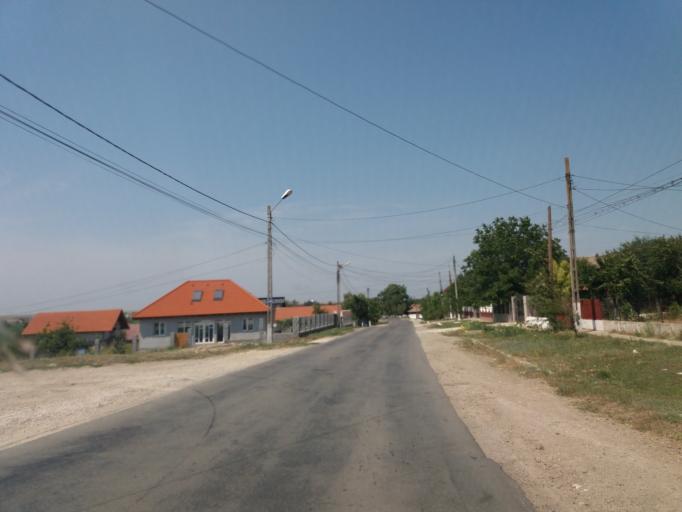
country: RO
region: Constanta
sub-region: Comuna Corbu
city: Corbu
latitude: 44.4056
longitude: 28.6615
